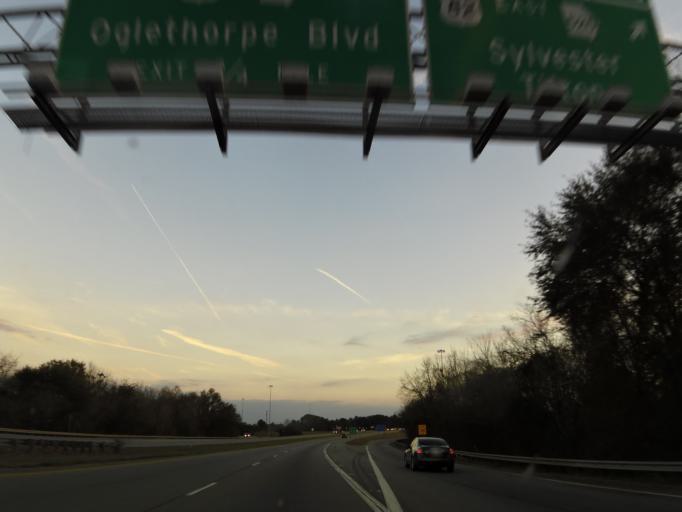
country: US
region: Georgia
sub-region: Dougherty County
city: Albany
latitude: 31.5854
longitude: -84.1133
